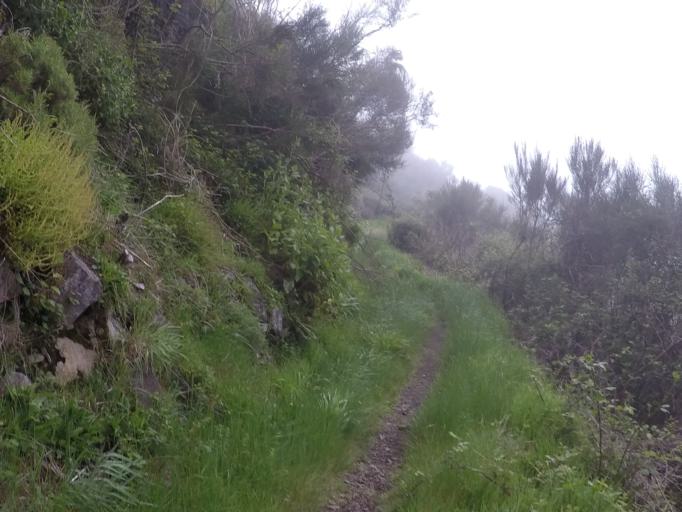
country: PT
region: Madeira
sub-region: Camara de Lobos
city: Curral das Freiras
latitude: 32.7325
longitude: -16.9863
